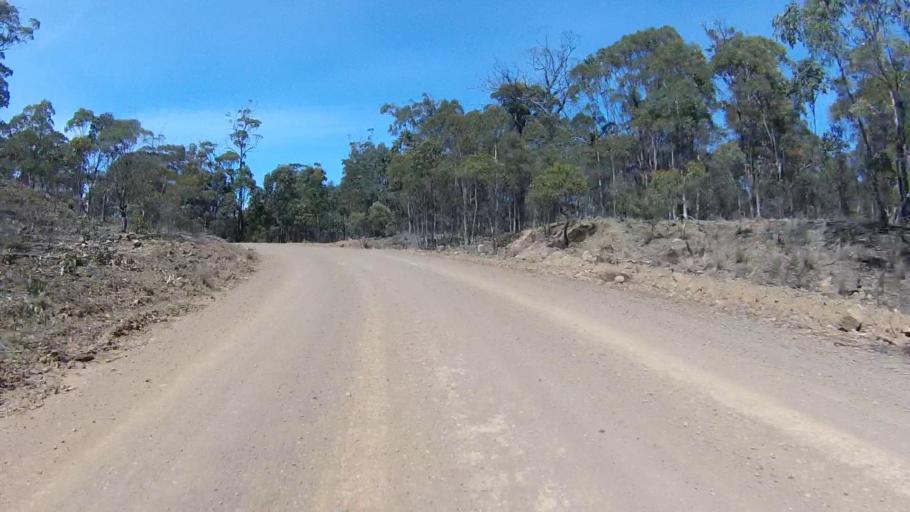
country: AU
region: Tasmania
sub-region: Sorell
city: Sorell
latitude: -42.6727
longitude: 147.7261
